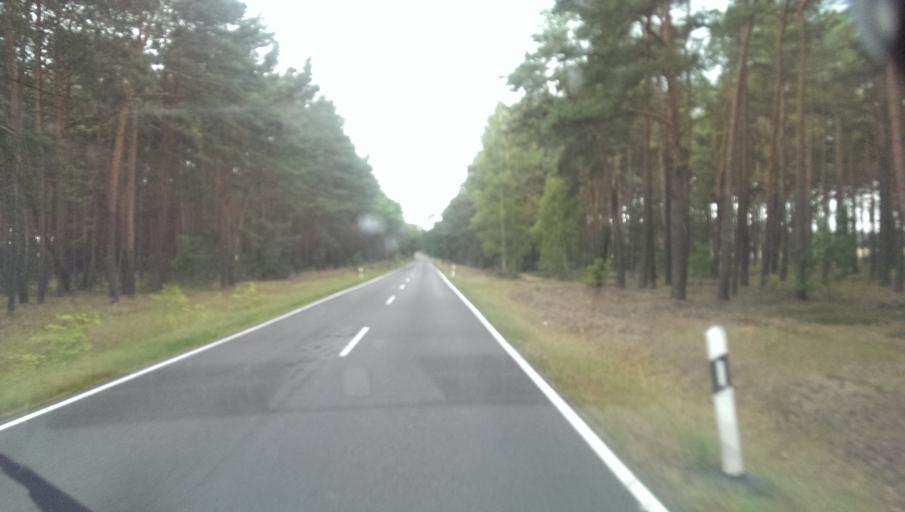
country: DE
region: Brandenburg
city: Borkwalde
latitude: 52.2930
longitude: 12.8173
